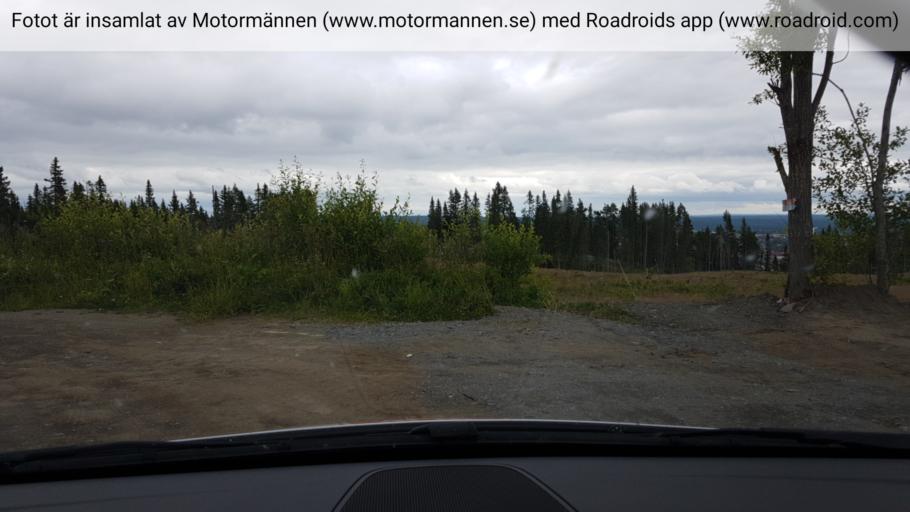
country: SE
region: Jaemtland
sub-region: OEstersunds Kommun
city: Ostersund
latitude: 63.1821
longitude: 14.5972
